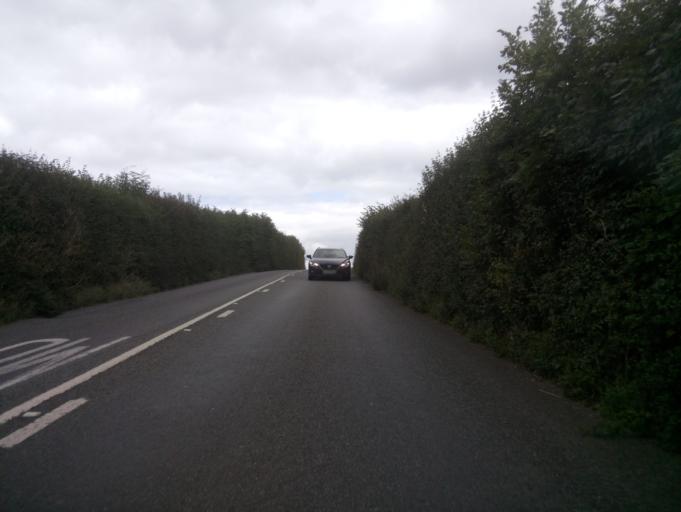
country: GB
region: England
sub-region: Devon
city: Bishopsteignton
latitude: 50.5495
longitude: -3.5541
